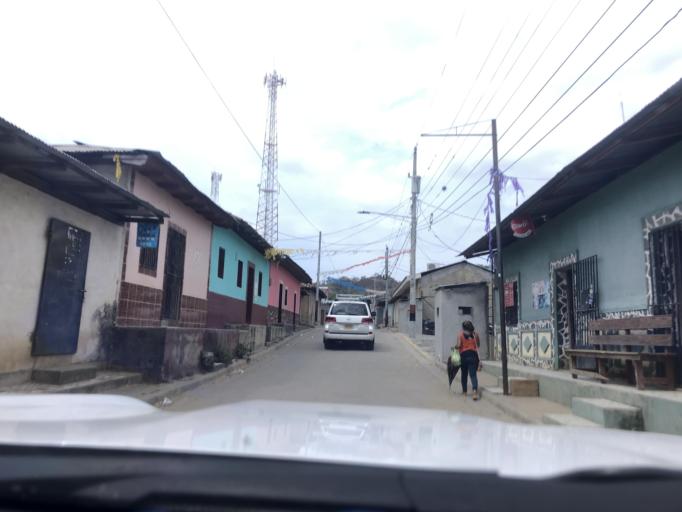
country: HN
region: El Paraiso
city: Oropoli
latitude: 13.7469
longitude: -86.7088
